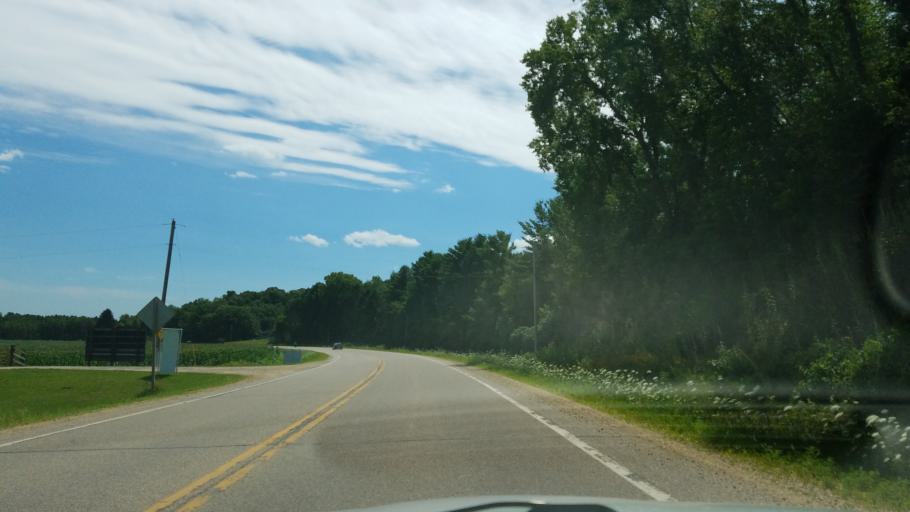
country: US
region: Wisconsin
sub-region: Saint Croix County
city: Glenwood City
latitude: 45.0521
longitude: -92.1773
